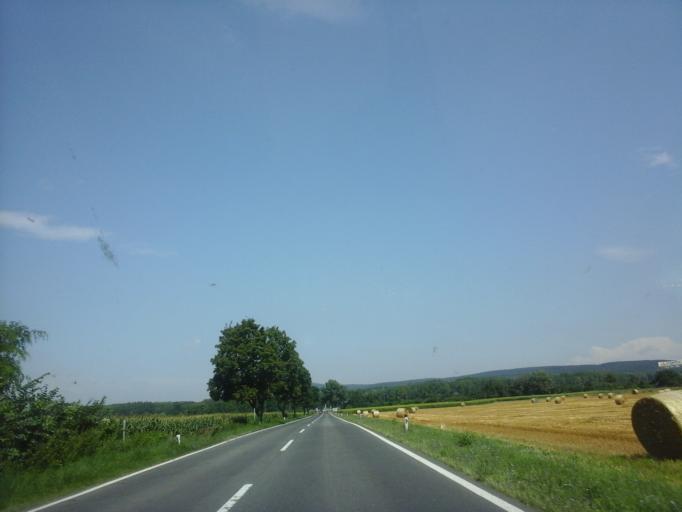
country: AT
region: Lower Austria
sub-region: Politischer Bezirk Bruck an der Leitha
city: Berg
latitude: 48.1220
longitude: 17.0324
